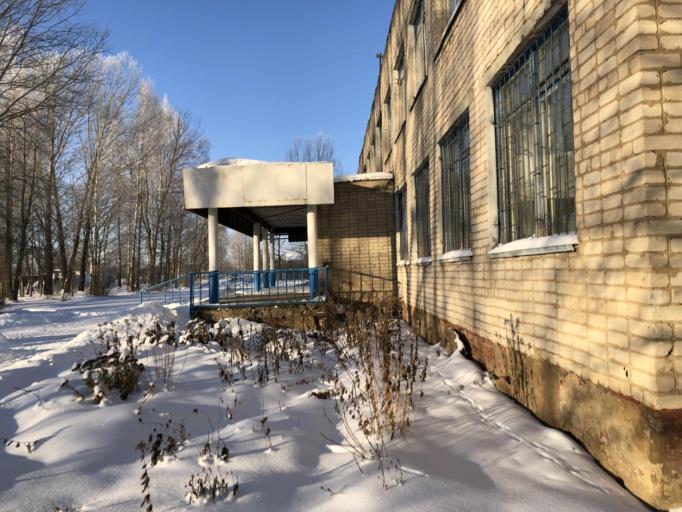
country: RU
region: Smolensk
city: Safonovo
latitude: 55.0862
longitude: 33.0702
